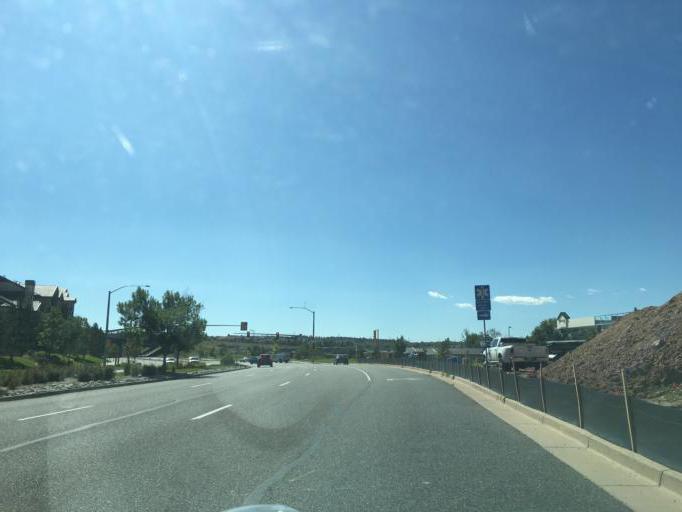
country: US
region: Colorado
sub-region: Douglas County
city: Parker
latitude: 39.5919
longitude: -104.7218
